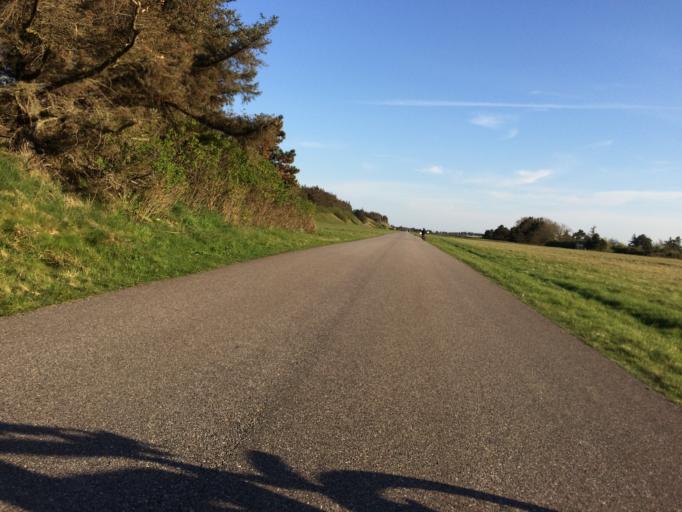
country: DK
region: Central Jutland
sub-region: Struer Kommune
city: Struer
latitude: 56.5345
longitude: 8.6275
